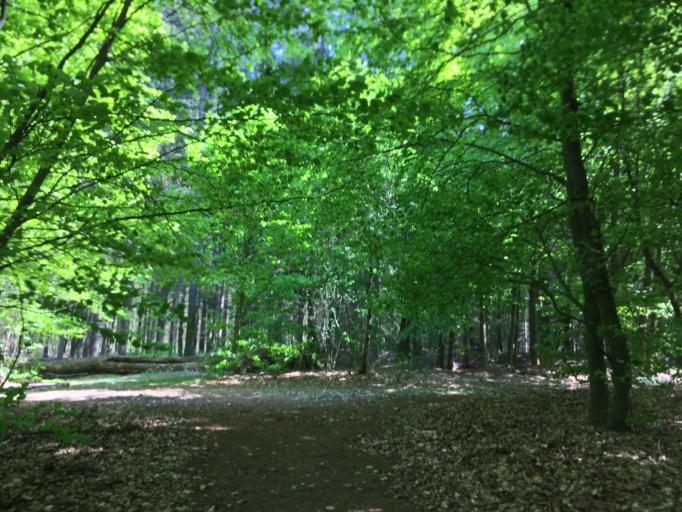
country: DE
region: Brandenburg
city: Wandlitz
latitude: 52.7407
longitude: 13.5077
